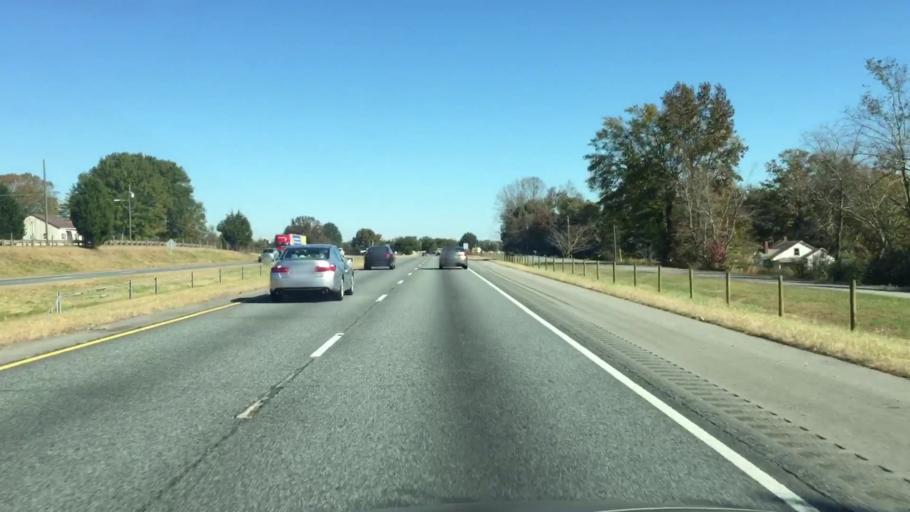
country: US
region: North Carolina
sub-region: Rockingham County
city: Reidsville
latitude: 36.2507
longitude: -79.6624
